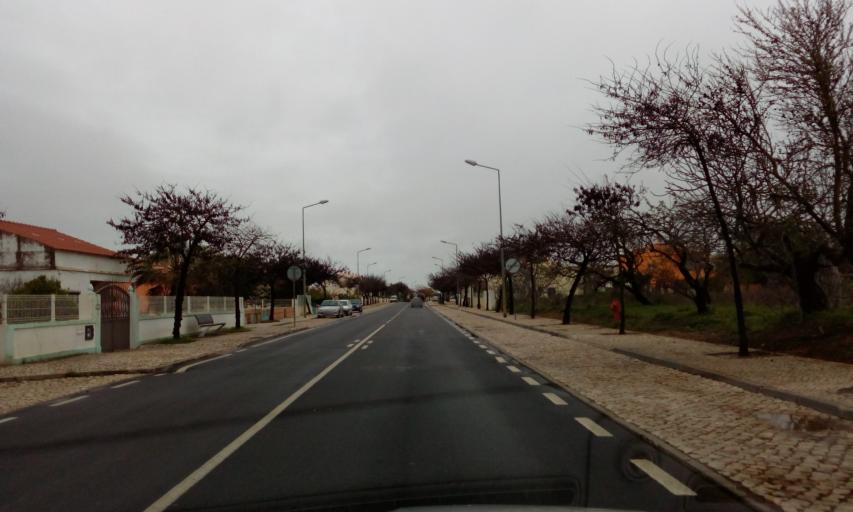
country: PT
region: Faro
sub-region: Albufeira
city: Ferreiras
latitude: 37.1248
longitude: -8.2280
